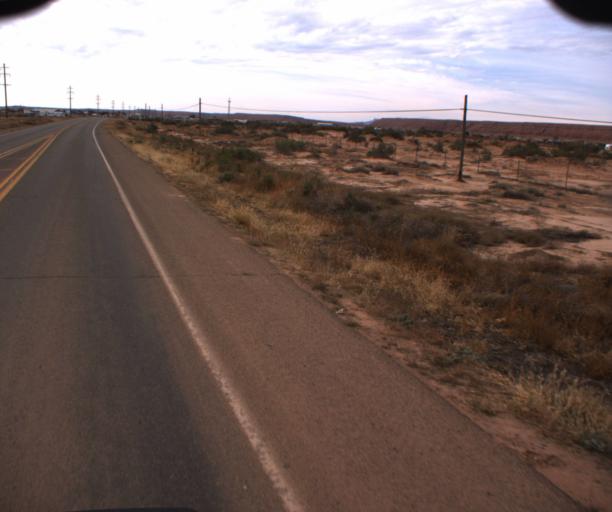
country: US
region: Arizona
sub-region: Apache County
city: Many Farms
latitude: 36.3620
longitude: -109.6145
